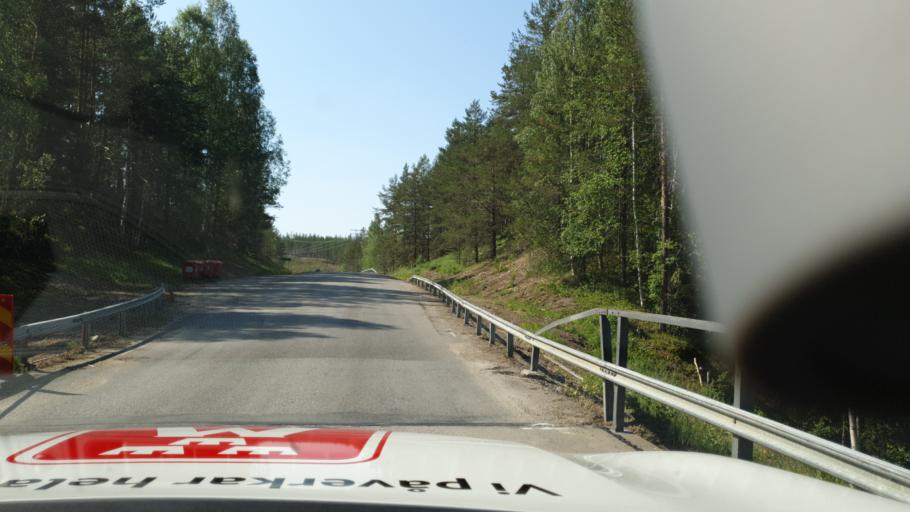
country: SE
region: Vaesterbotten
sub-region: Skelleftea Kommun
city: Langsele
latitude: 64.9438
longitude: 20.0351
